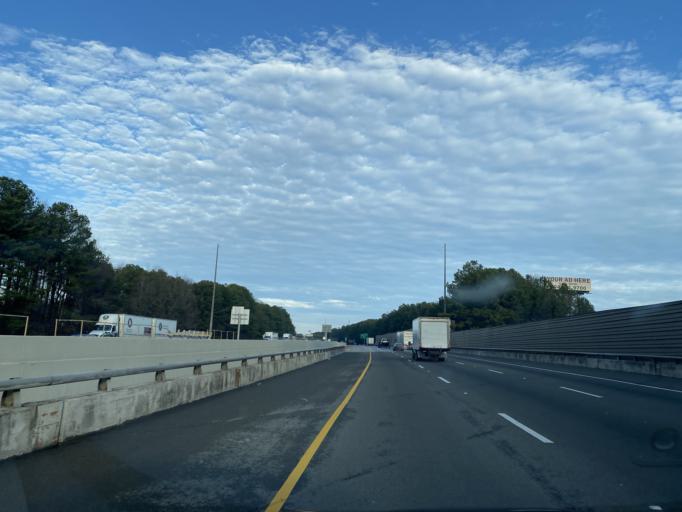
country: US
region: Georgia
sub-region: Cobb County
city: Kennesaw
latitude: 34.0435
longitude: -84.5804
